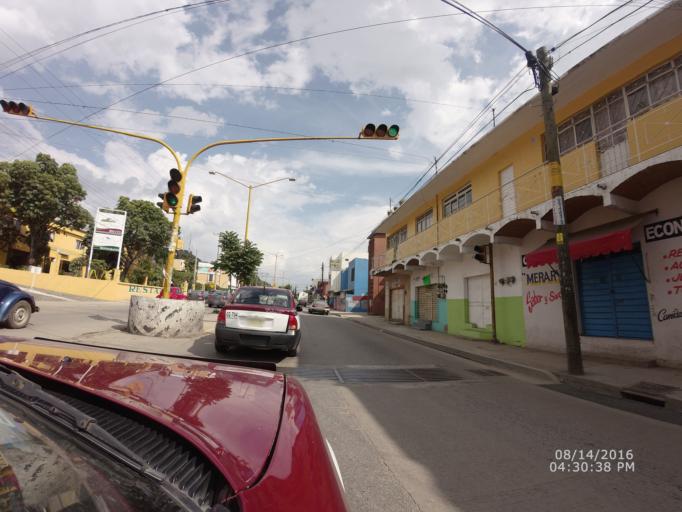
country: MX
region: Oaxaca
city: Oaxaca de Juarez
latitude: 17.0775
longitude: -96.7420
